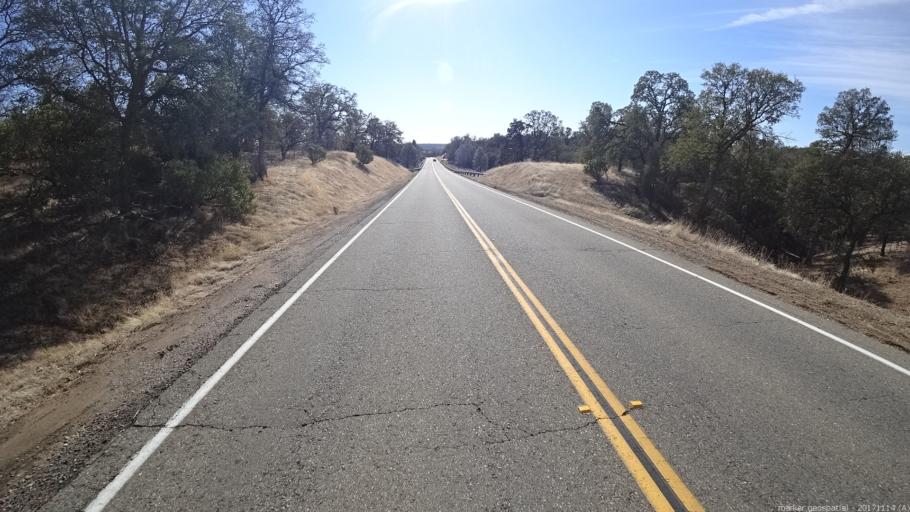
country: US
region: California
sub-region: Shasta County
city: Anderson
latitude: 40.4051
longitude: -122.4063
